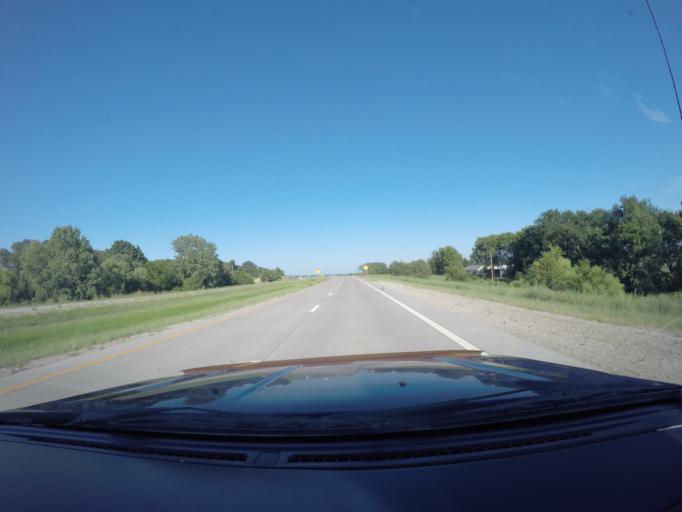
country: US
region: Kansas
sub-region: Shawnee County
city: Topeka
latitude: 39.0869
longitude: -95.4874
